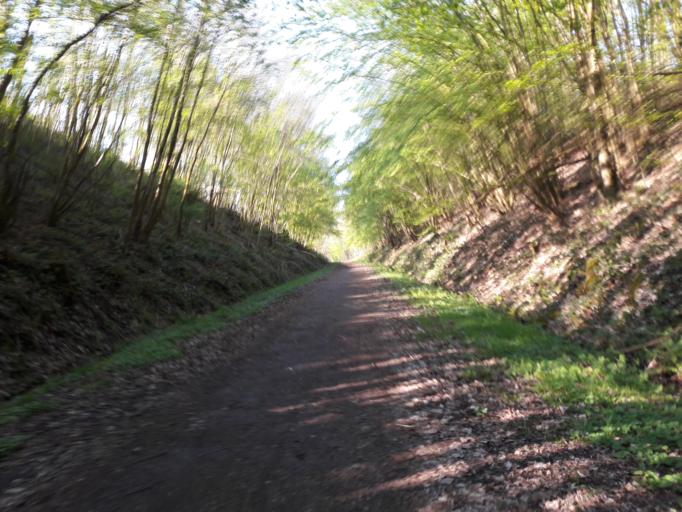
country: FR
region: Nord-Pas-de-Calais
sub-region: Departement du Nord
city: Sains-du-Nord
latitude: 50.1426
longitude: 4.0676
